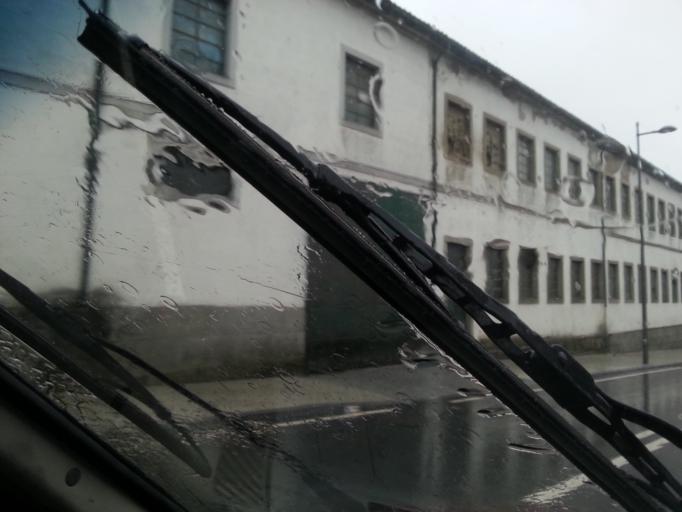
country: PT
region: Guarda
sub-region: Guarda
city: Guarda
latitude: 40.5393
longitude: -7.2751
